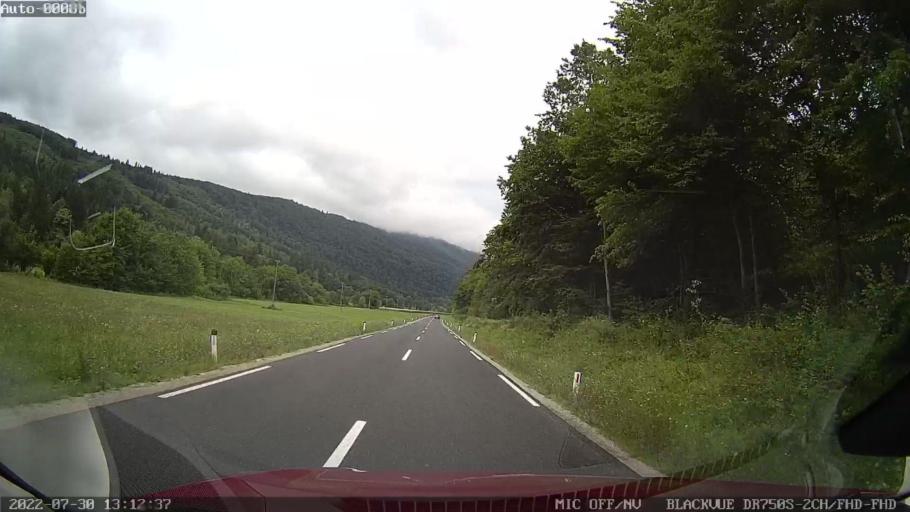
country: SI
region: Dolenjske Toplice
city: Dolenjske Toplice
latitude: 45.7141
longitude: 15.0680
